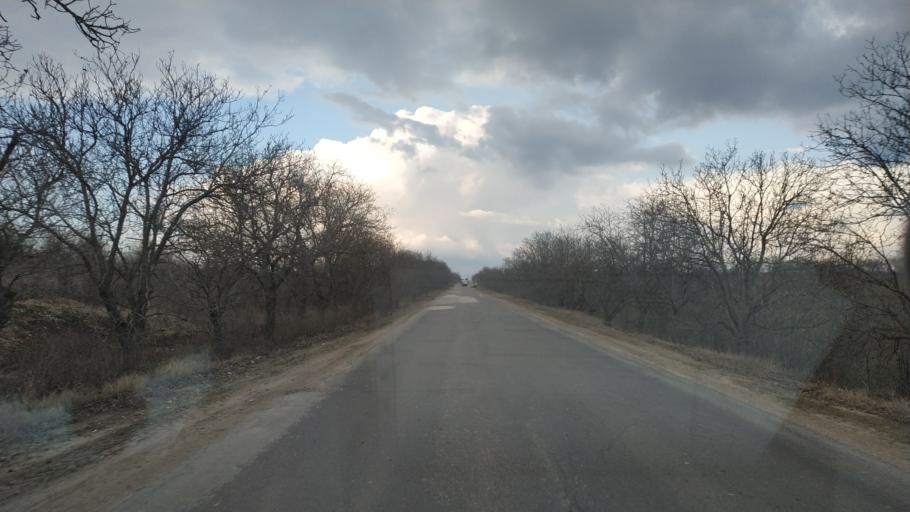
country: MD
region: Anenii Noi
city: Anenii Noi
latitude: 46.9546
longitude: 29.2829
